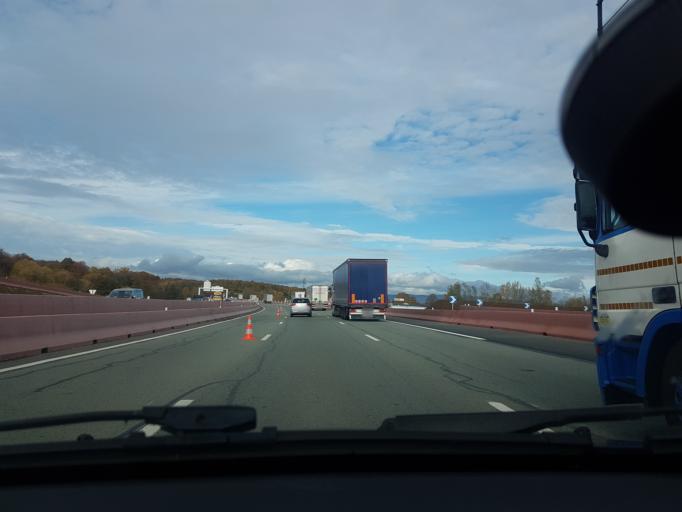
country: FR
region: Franche-Comte
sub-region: Territoire de Belfort
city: Andelnans
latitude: 47.5922
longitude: 6.8576
